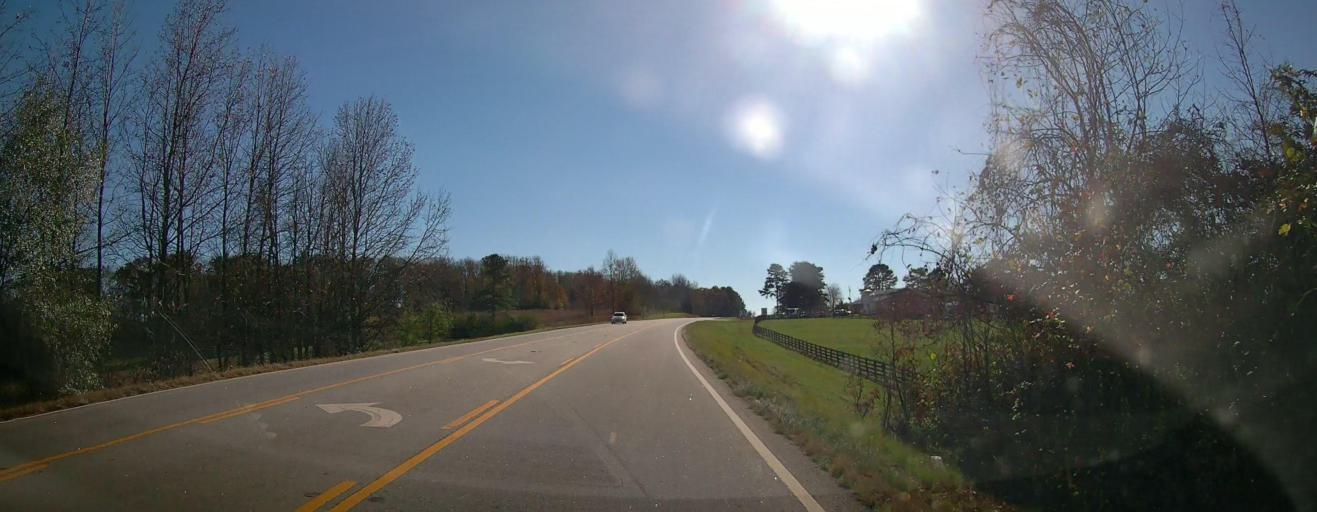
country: US
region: Georgia
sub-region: White County
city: Cleveland
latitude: 34.4933
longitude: -83.7564
